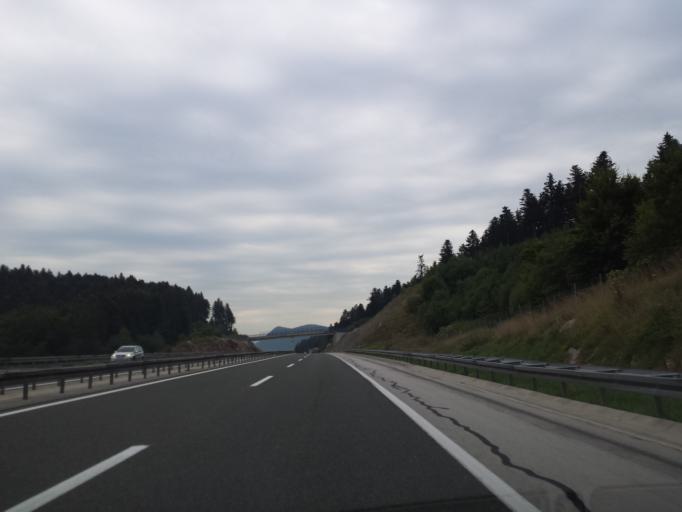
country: HR
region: Licko-Senjska
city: Otocac
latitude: 44.8510
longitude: 15.2292
